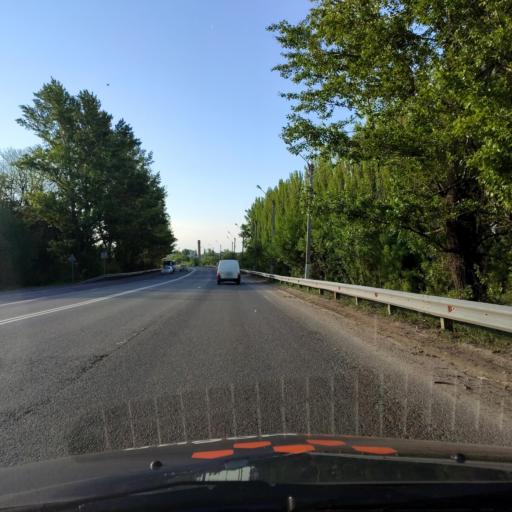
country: RU
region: Lipetsk
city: Yelets
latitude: 52.5993
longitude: 38.4739
